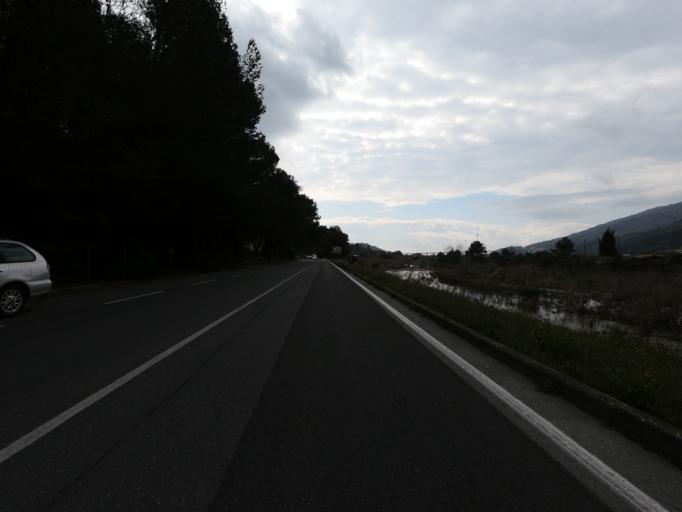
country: IT
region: Liguria
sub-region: Provincia di Savona
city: Laigueglia
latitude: 43.9830
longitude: 8.1331
